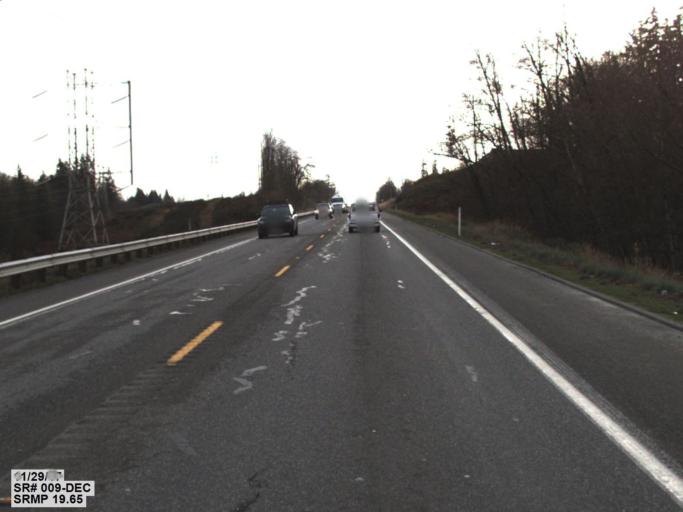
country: US
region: Washington
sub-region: Snohomish County
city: Sisco Heights
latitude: 48.0590
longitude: -122.1110
